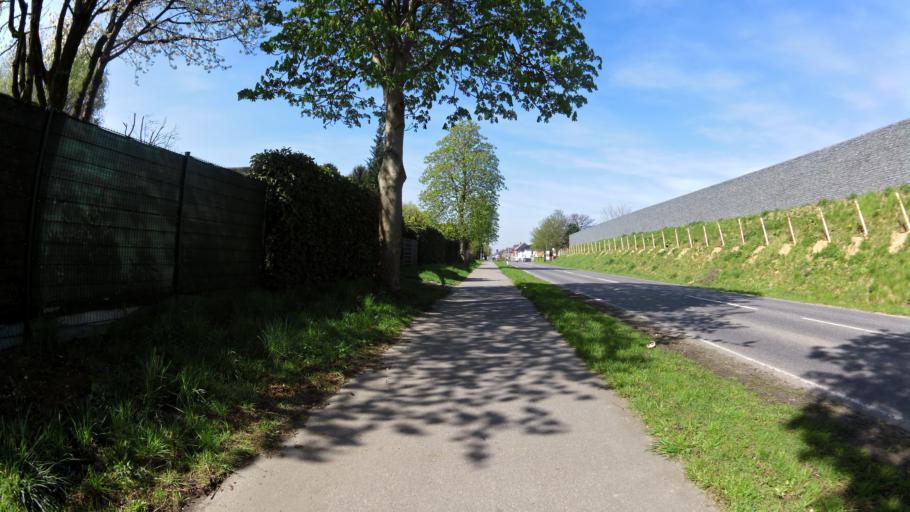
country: DE
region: North Rhine-Westphalia
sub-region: Regierungsbezirk Koln
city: Ubach-Palenberg
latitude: 50.9126
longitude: 6.1488
